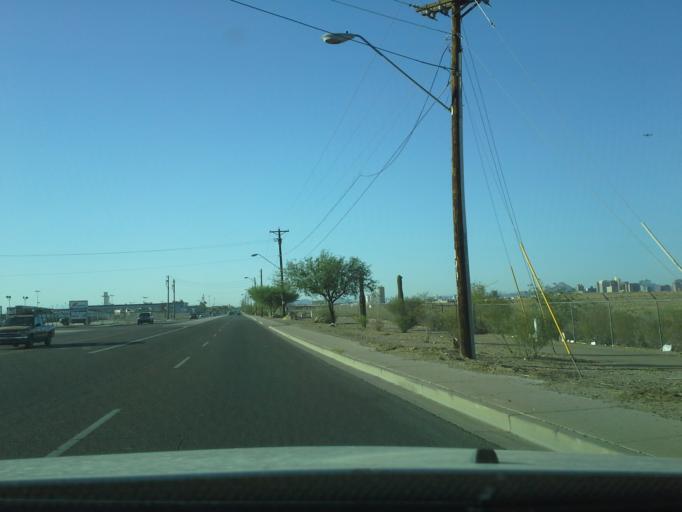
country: US
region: Arizona
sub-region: Maricopa County
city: Phoenix
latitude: 33.4126
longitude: -112.0994
